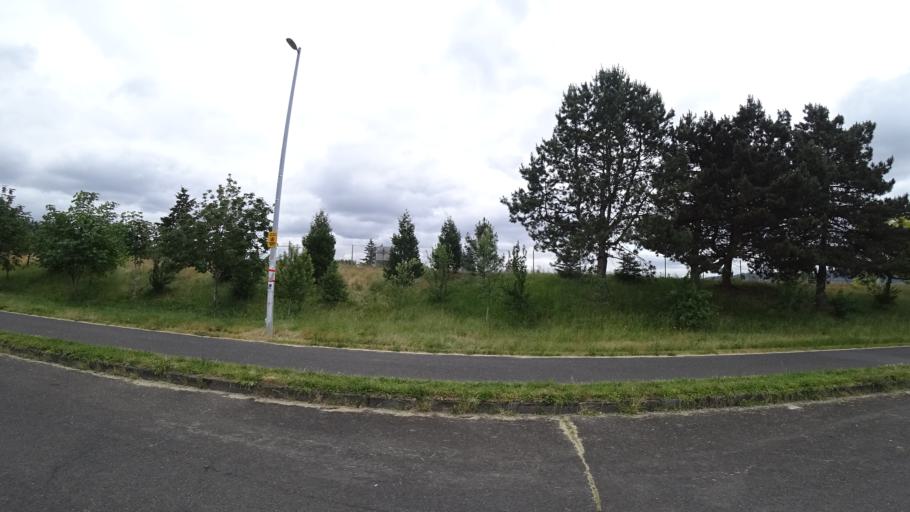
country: US
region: Oregon
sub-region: Multnomah County
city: Lents
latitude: 45.4919
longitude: -122.5672
